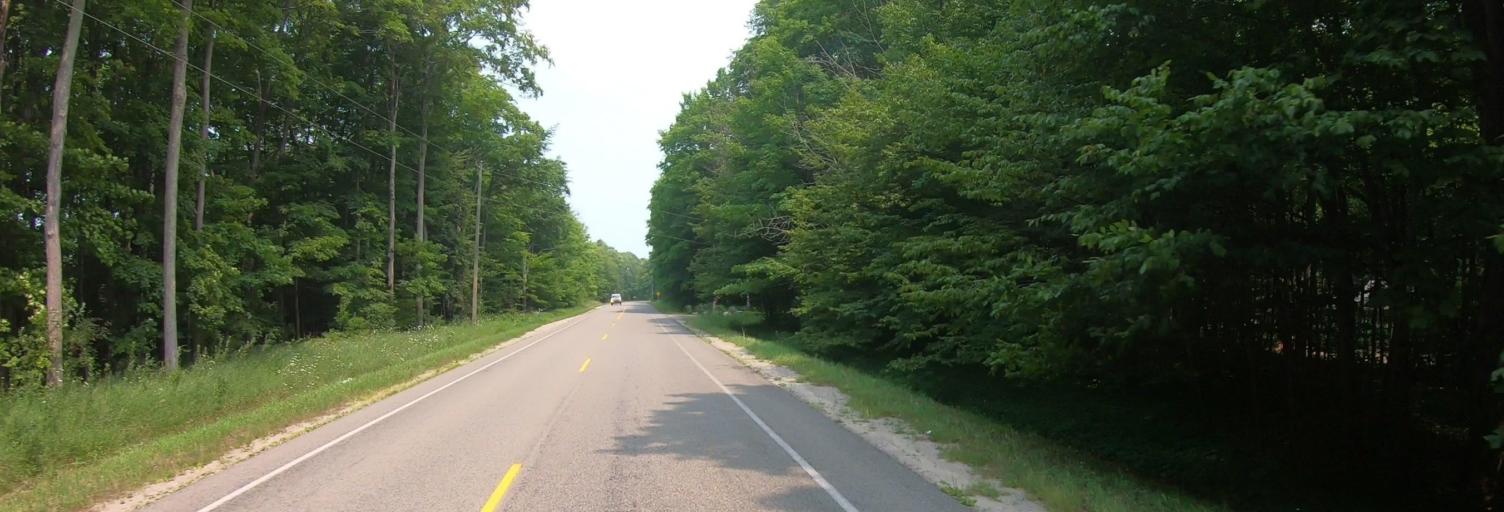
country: US
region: Michigan
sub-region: Leelanau County
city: Leland
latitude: 45.1562
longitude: -85.5900
